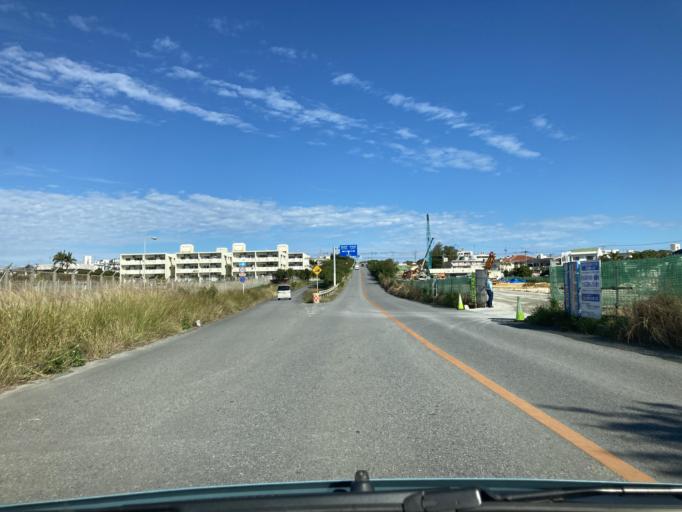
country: JP
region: Okinawa
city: Okinawa
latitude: 26.3782
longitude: 127.7455
